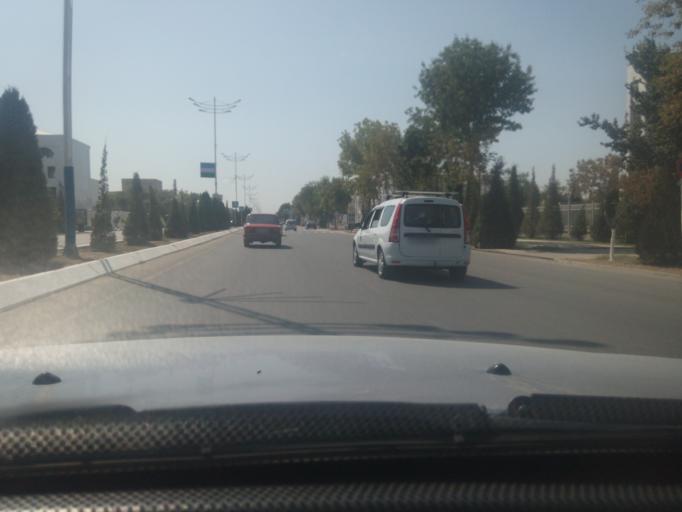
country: UZ
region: Sirdaryo
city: Guliston
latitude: 40.4979
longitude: 68.7746
